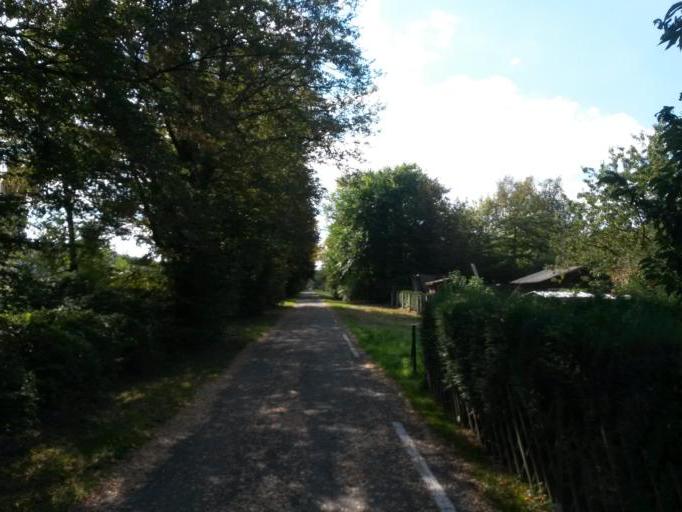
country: DE
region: Baden-Wuerttemberg
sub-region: Karlsruhe Region
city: Otisheim
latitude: 48.9379
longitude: 8.8064
